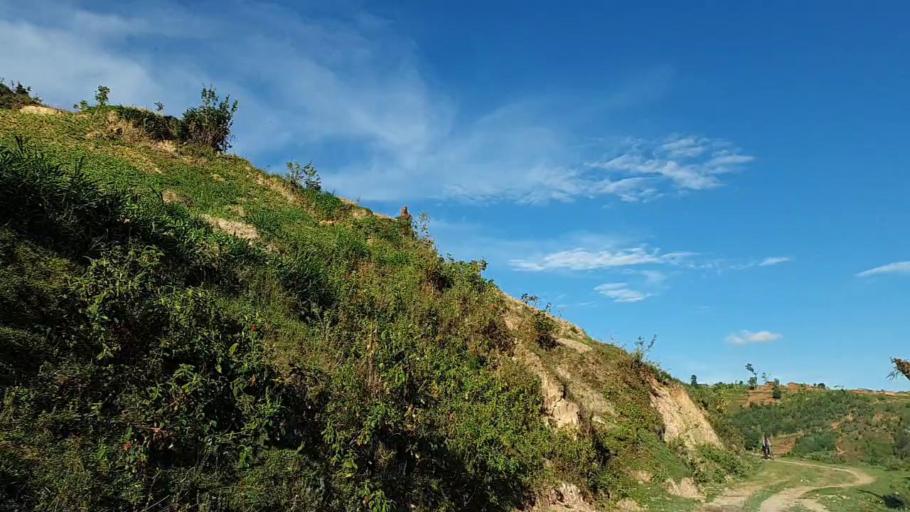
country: RW
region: Southern Province
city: Nzega
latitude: -2.4177
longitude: 29.5135
